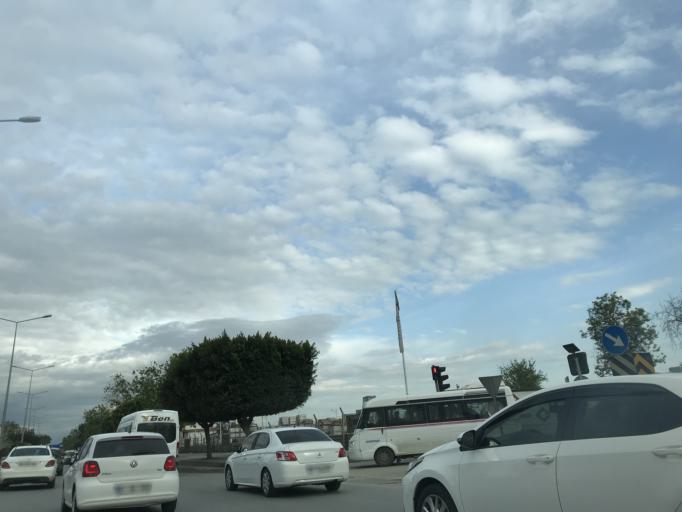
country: TR
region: Adana
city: Seyhan
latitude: 36.9942
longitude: 35.2878
